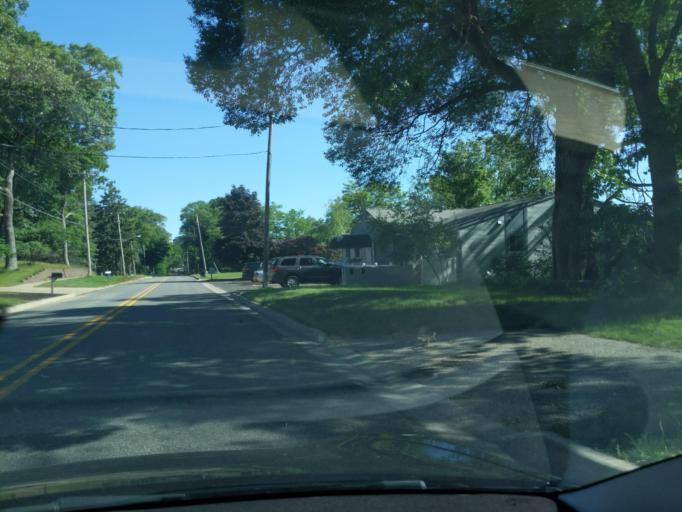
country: US
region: Michigan
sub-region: Muskegon County
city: Montague
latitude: 43.4065
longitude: -86.3600
